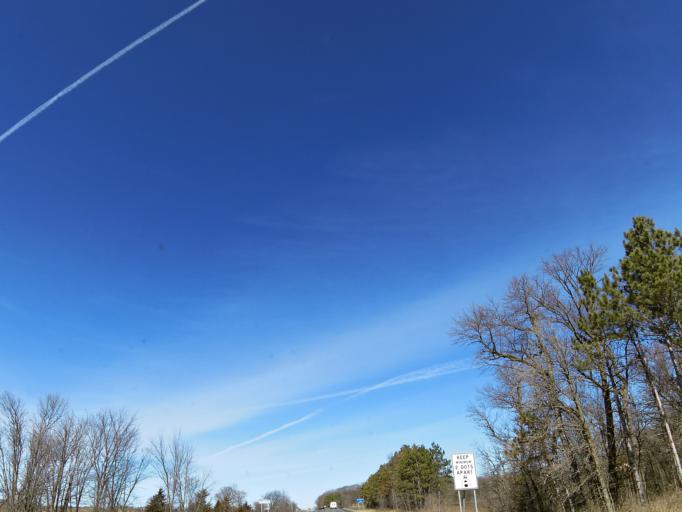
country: US
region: Minnesota
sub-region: Wright County
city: Buffalo
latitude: 45.1258
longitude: -93.8170
